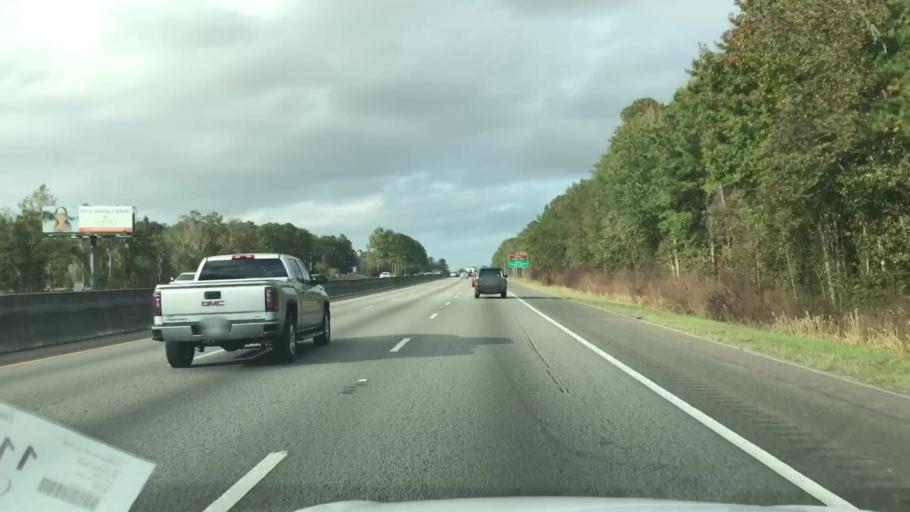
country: US
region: South Carolina
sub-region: Berkeley County
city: Ladson
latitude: 32.9697
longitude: -80.0754
